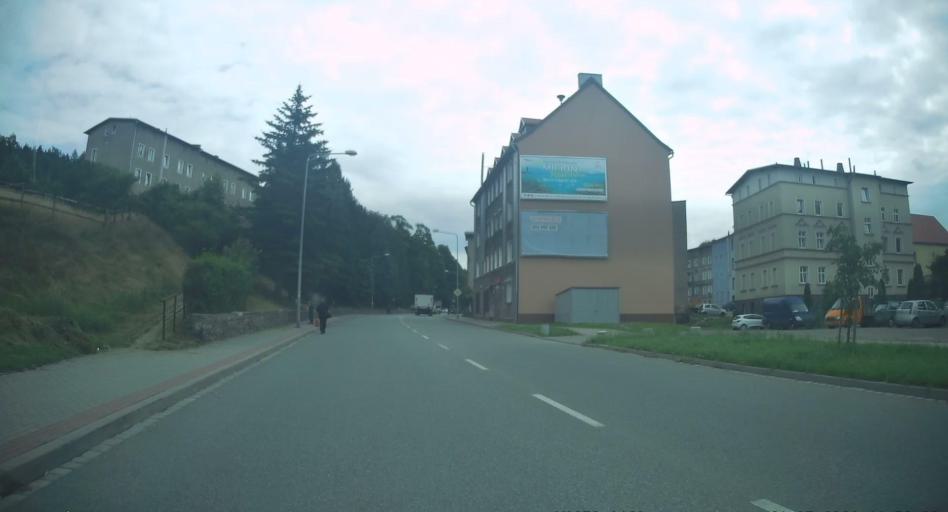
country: PL
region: Lower Silesian Voivodeship
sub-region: Powiat walbrzyski
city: Walbrzych
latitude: 50.7711
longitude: 16.3053
